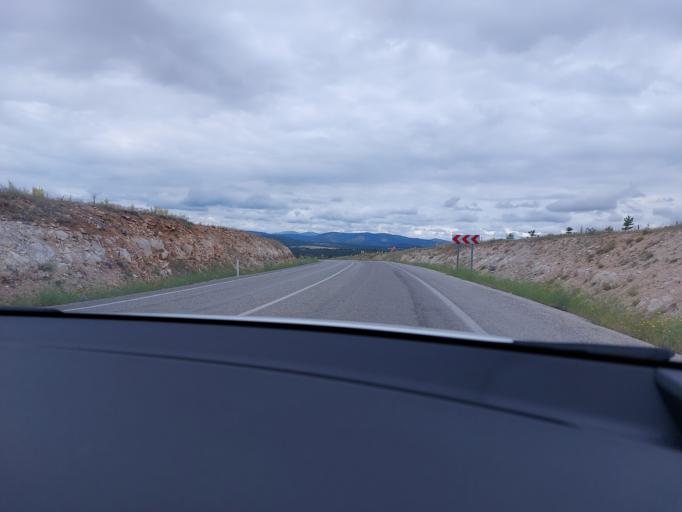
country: TR
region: Konya
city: Doganbey
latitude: 37.8828
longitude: 31.8385
